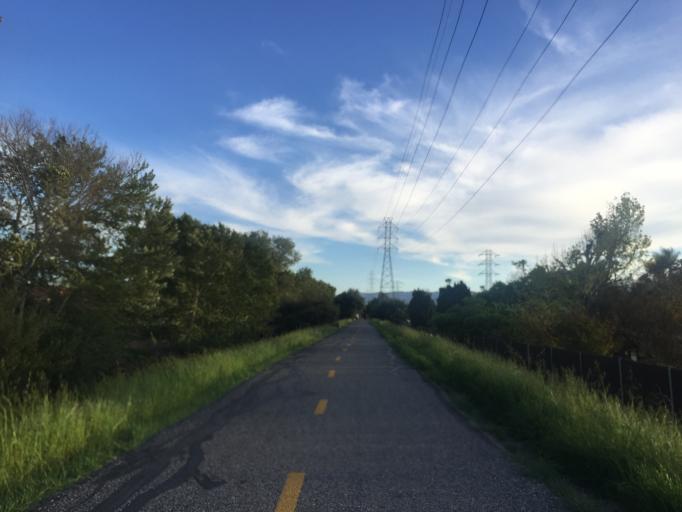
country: US
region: California
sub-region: Santa Clara County
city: Mountain View
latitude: 37.4170
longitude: -122.0689
